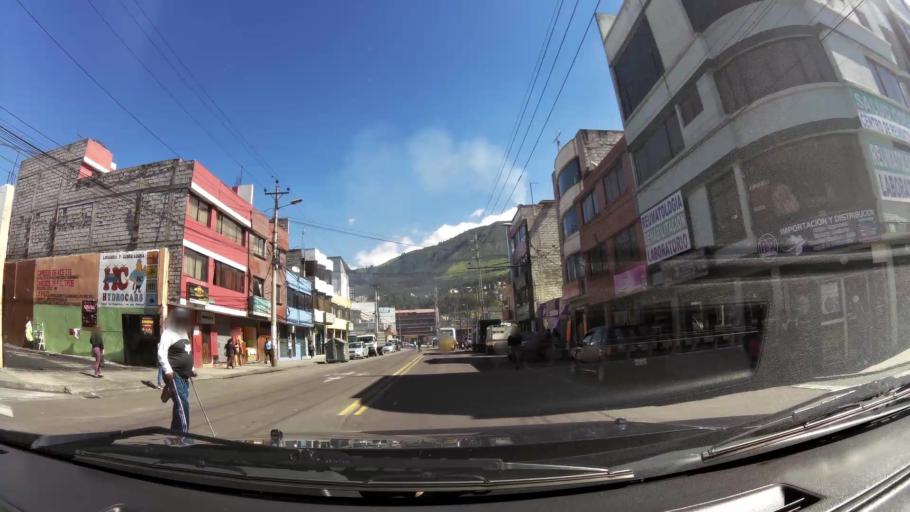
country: EC
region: Pichincha
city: Quito
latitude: -0.2575
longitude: -78.5420
